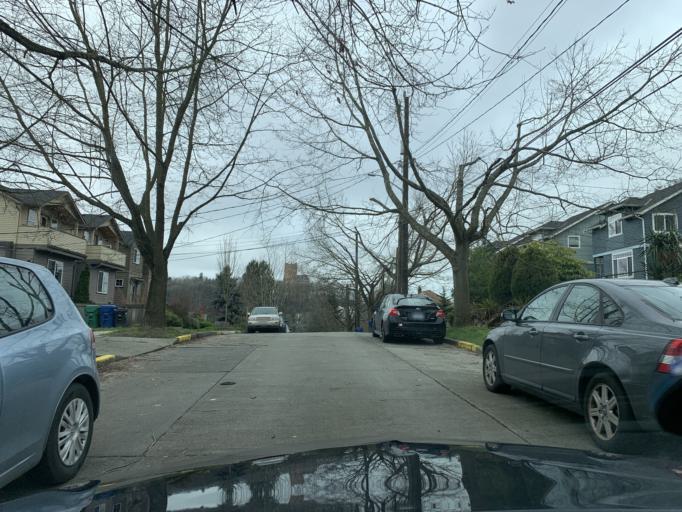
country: US
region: Washington
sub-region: King County
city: Seattle
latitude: 47.5930
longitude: -122.3049
